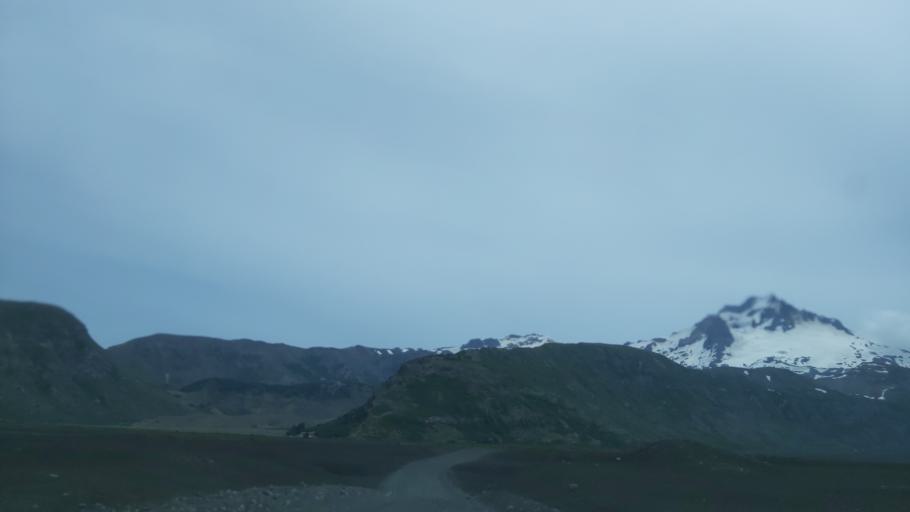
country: AR
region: Neuquen
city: Andacollo
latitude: -37.4605
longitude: -71.3074
